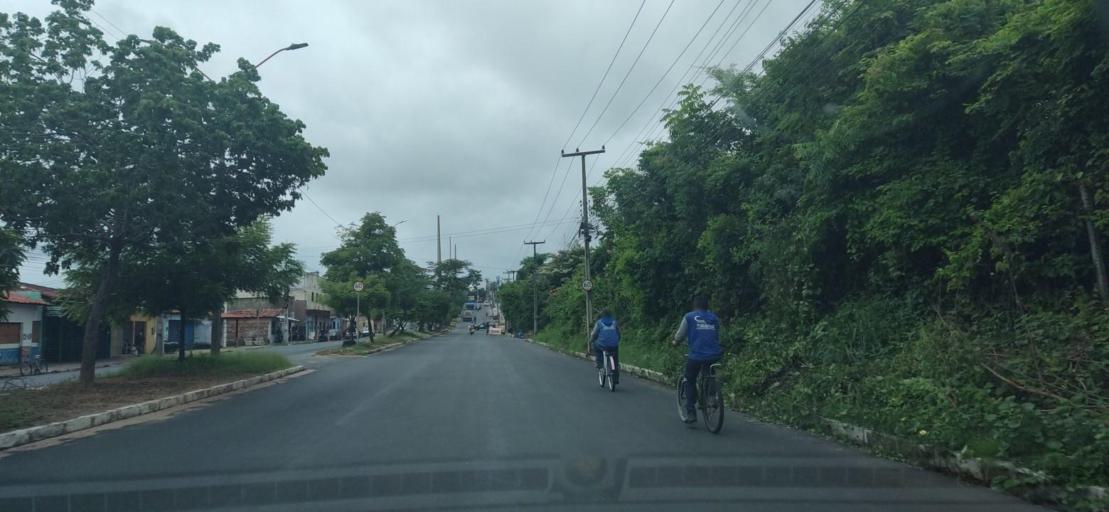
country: BR
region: Piaui
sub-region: Teresina
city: Teresina
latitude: -5.0600
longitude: -42.7488
